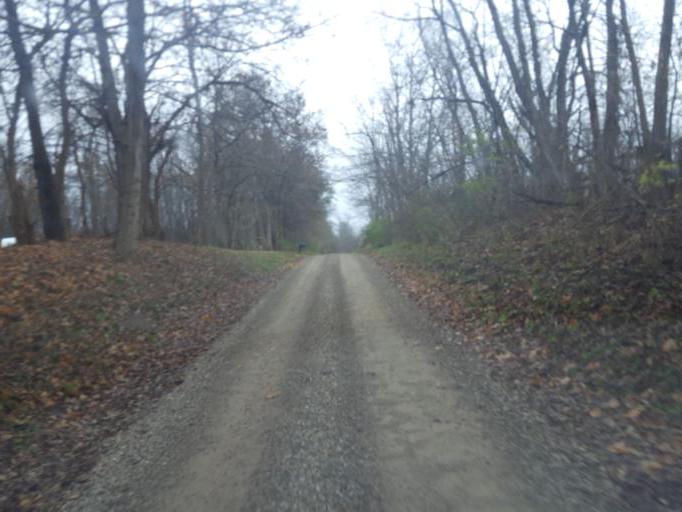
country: US
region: Ohio
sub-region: Knox County
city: Fredericktown
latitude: 40.4090
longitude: -82.6103
